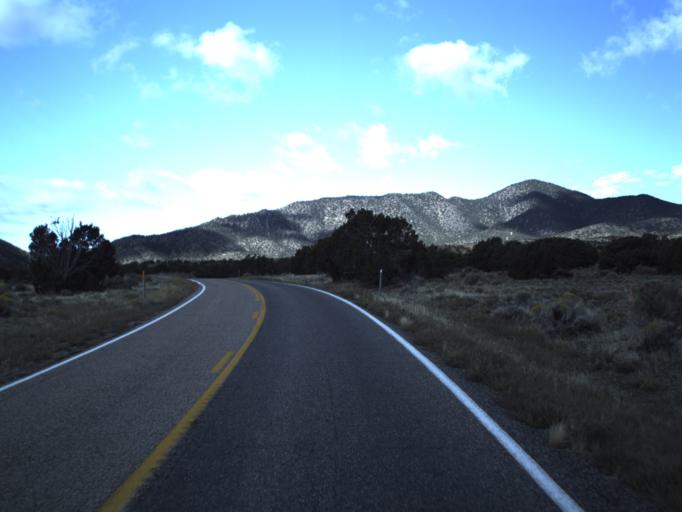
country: US
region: Utah
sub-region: Beaver County
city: Milford
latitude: 38.4616
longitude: -113.2471
